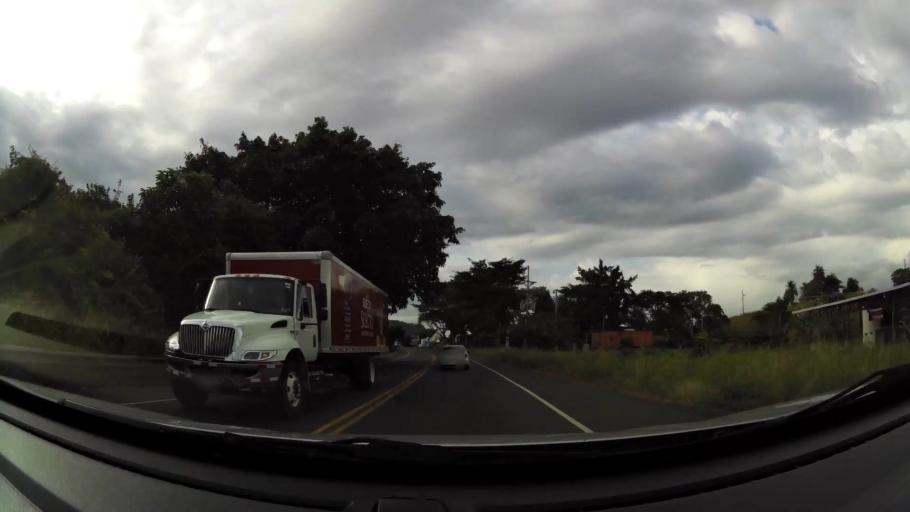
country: CR
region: Puntarenas
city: Esparza
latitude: 9.9050
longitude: -84.6610
